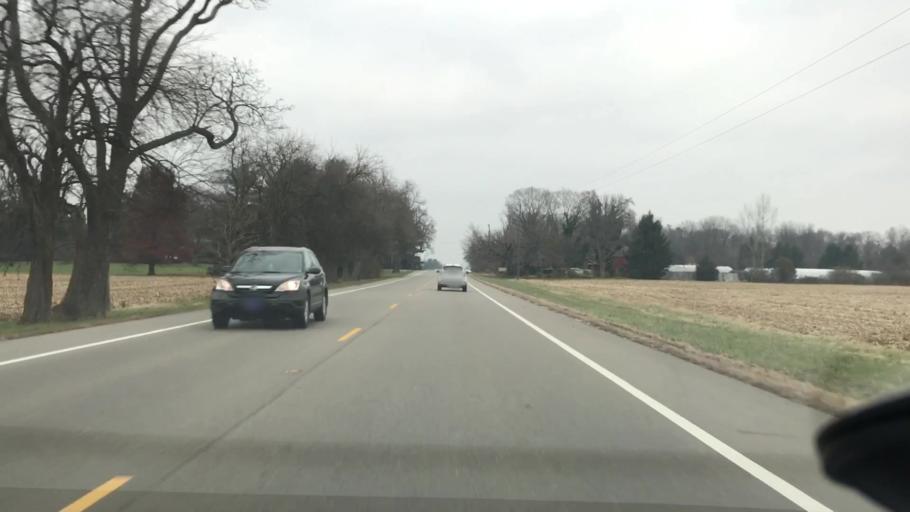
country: US
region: Ohio
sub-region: Greene County
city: Yellow Springs
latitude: 39.8159
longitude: -83.8787
